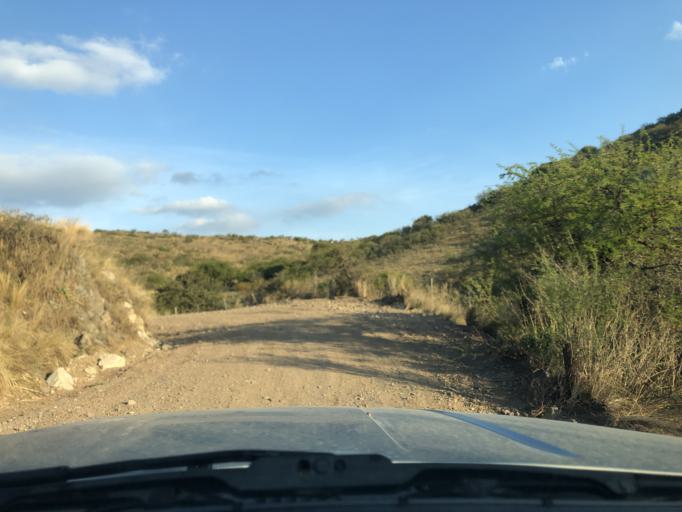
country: AR
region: Cordoba
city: Agua de Oro
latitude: -31.0554
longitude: -64.3535
